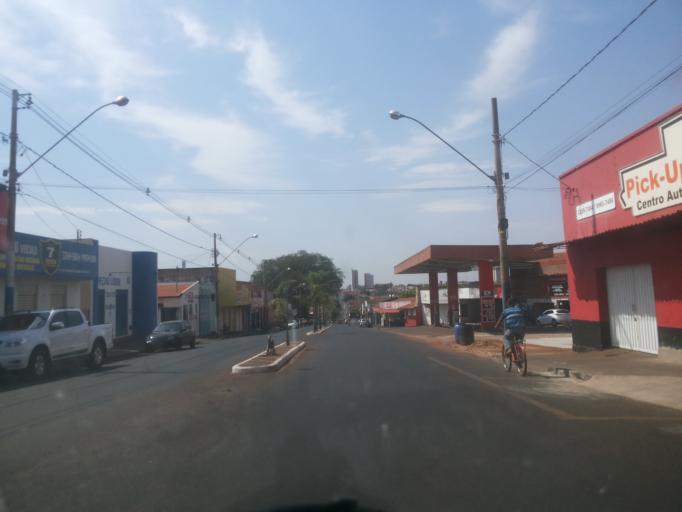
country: BR
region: Minas Gerais
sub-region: Ituiutaba
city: Ituiutaba
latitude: -18.9774
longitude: -49.4744
